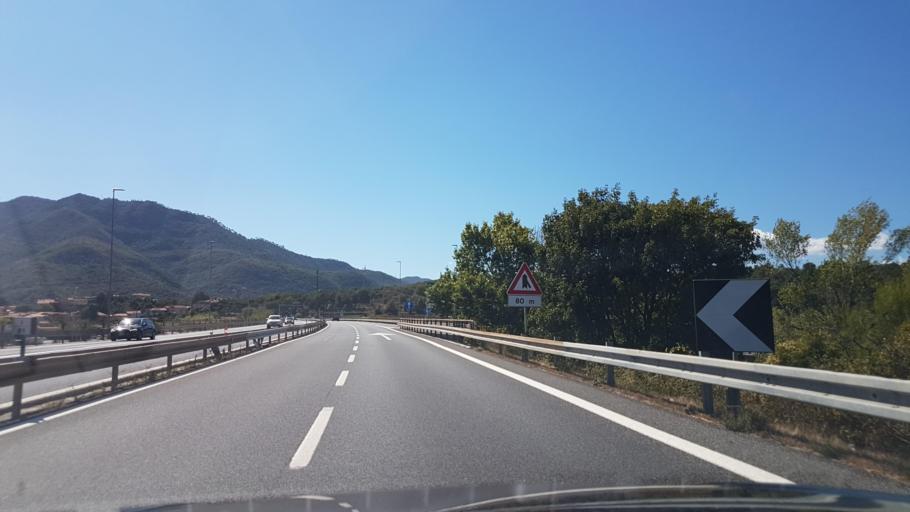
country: IT
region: Liguria
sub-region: Provincia di Savona
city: San Fedele-Lusignano
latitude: 44.0656
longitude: 8.1740
